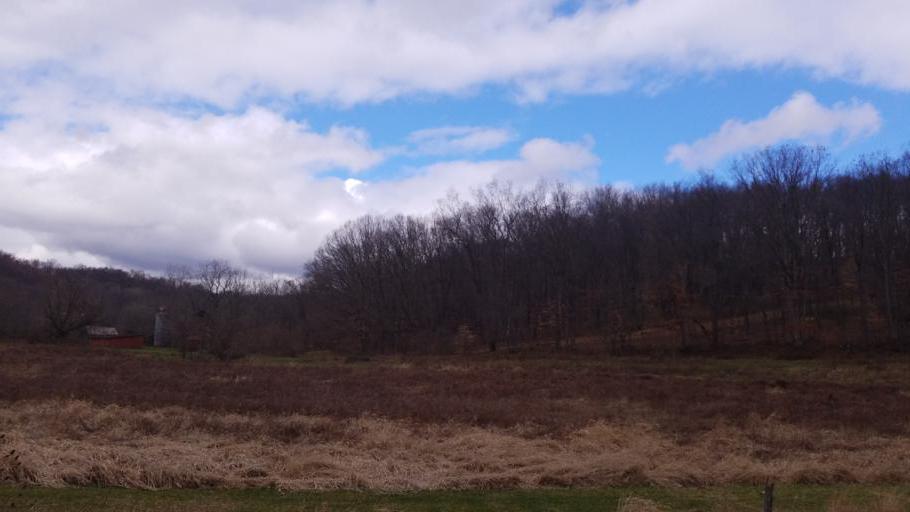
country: US
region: Ohio
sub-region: Muskingum County
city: Frazeysburg
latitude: 40.1020
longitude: -82.1827
